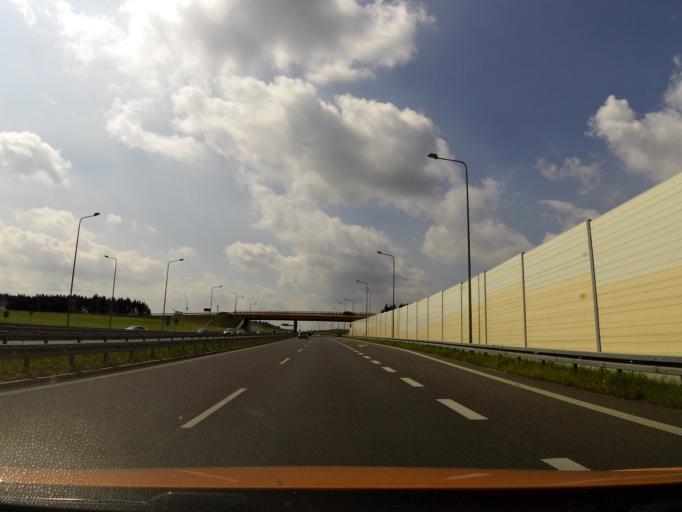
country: PL
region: West Pomeranian Voivodeship
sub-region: Powiat goleniowski
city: Nowogard
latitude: 53.6867
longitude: 15.0898
